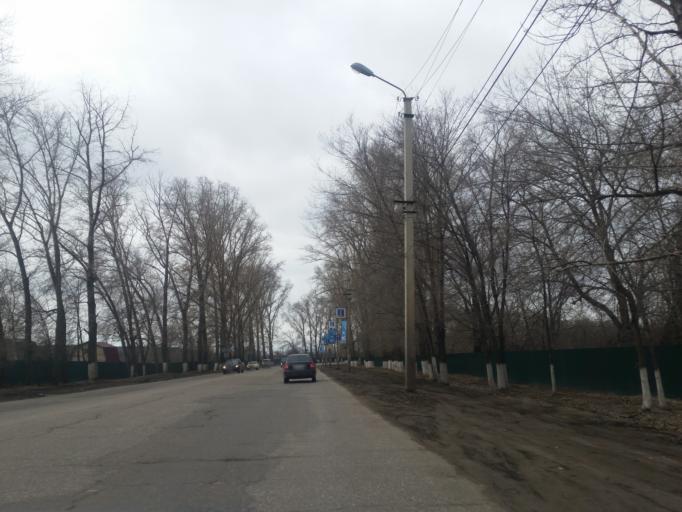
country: RU
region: Ulyanovsk
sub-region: Ulyanovskiy Rayon
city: Ulyanovsk
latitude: 54.3266
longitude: 48.4919
